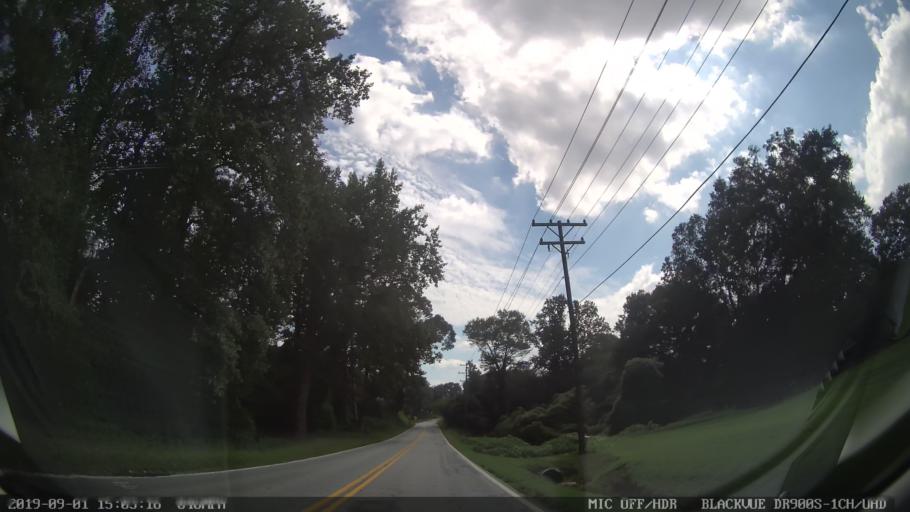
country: US
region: South Carolina
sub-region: Greenville County
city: Greer
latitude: 34.9653
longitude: -82.2013
